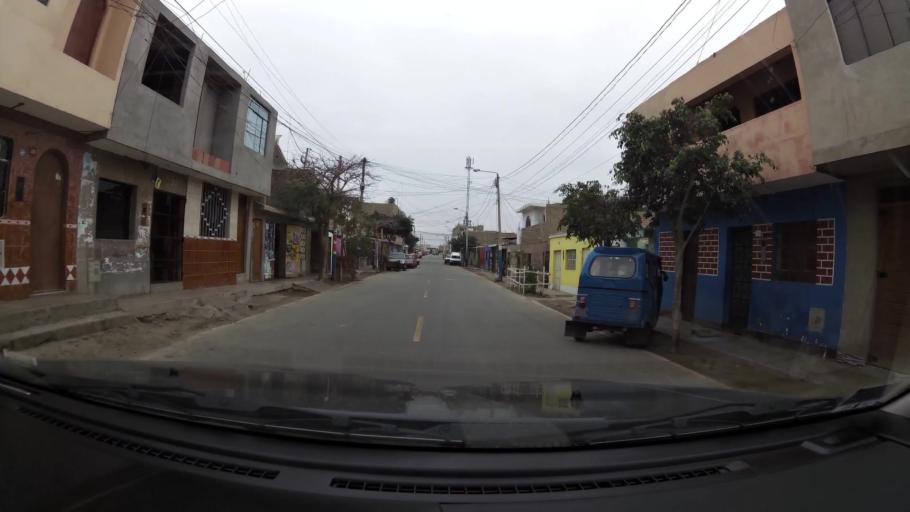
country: PE
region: Ica
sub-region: Provincia de Pisco
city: Pisco
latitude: -13.7143
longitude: -76.1983
